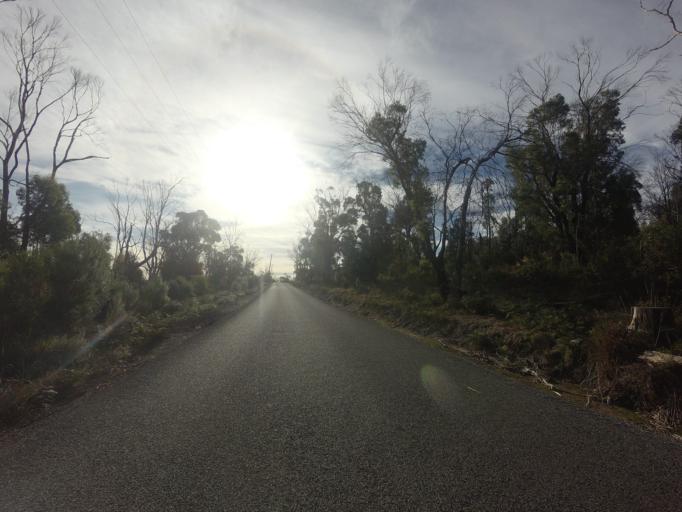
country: AU
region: Tasmania
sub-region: Sorell
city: Sorell
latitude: -42.9554
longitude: 147.8523
